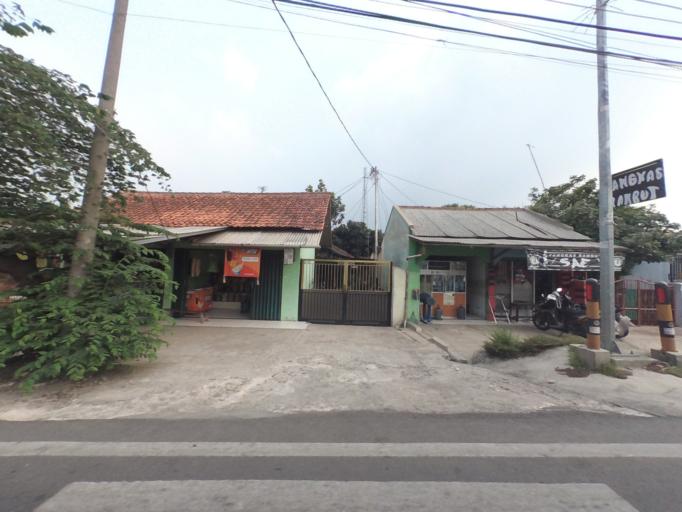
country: ID
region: West Java
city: Ciampea
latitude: -6.5668
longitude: 106.6723
